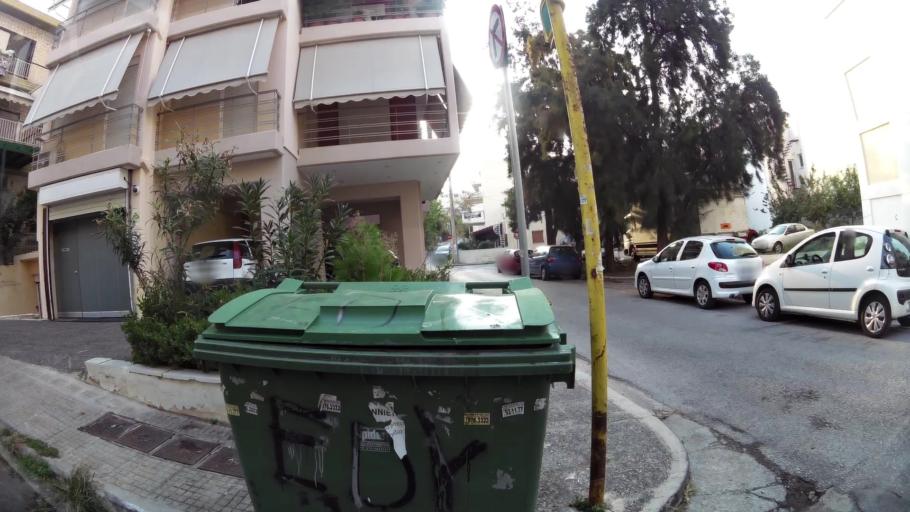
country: GR
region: Attica
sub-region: Nomarchia Athinas
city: Agios Dimitrios
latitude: 37.9397
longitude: 23.7241
